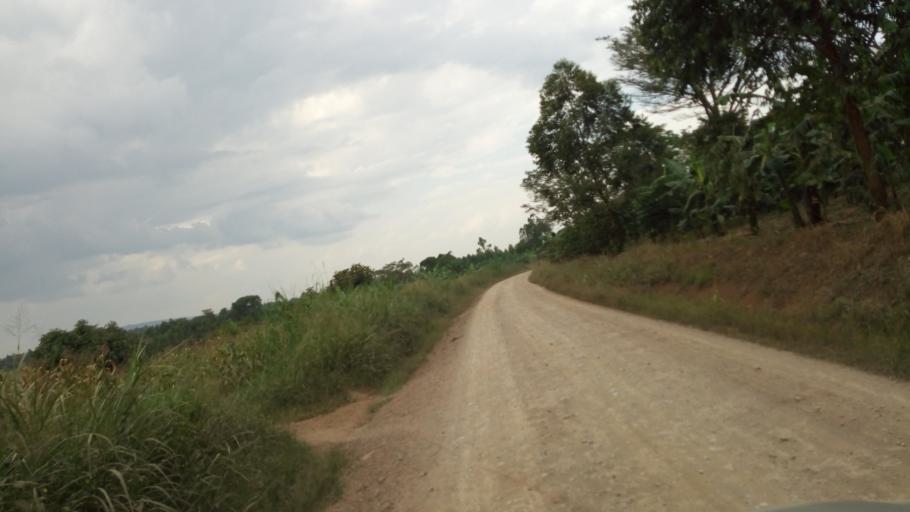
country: UG
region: Central Region
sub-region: Kiboga District
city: Kiboga
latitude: 0.7196
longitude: 31.7408
